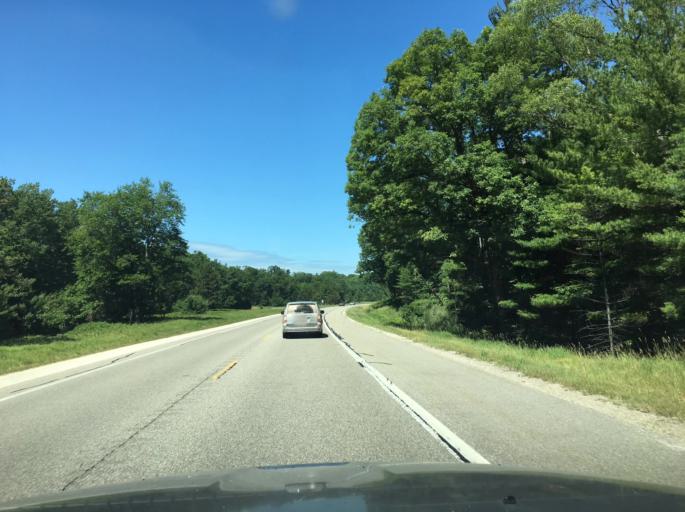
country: US
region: Michigan
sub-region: Osceola County
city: Reed City
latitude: 43.8932
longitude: -85.6782
